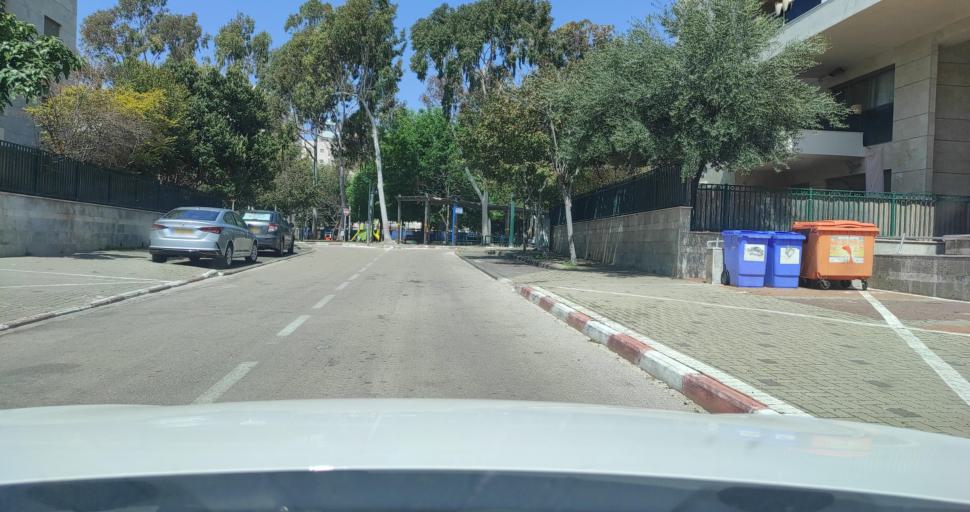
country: IL
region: Central District
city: Nordiyya
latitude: 32.3006
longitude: 34.8715
